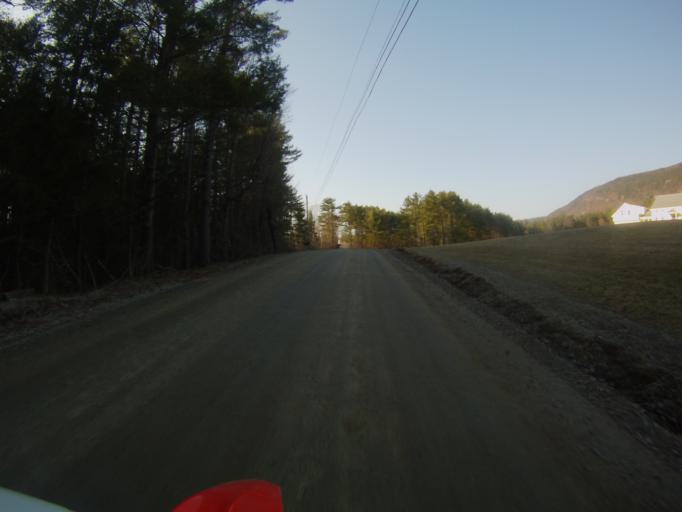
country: US
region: Vermont
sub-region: Addison County
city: Bristol
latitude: 44.0985
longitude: -73.0875
